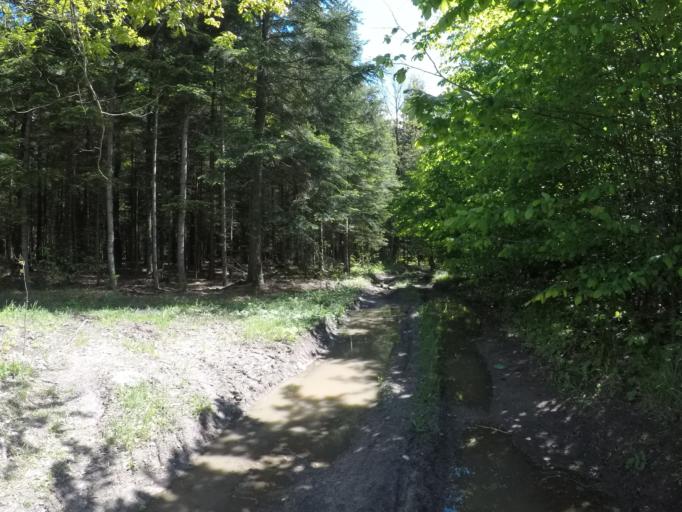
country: PL
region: Swietokrzyskie
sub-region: Powiat kielecki
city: Kostomloty Pierwsze
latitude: 50.9250
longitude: 20.6328
